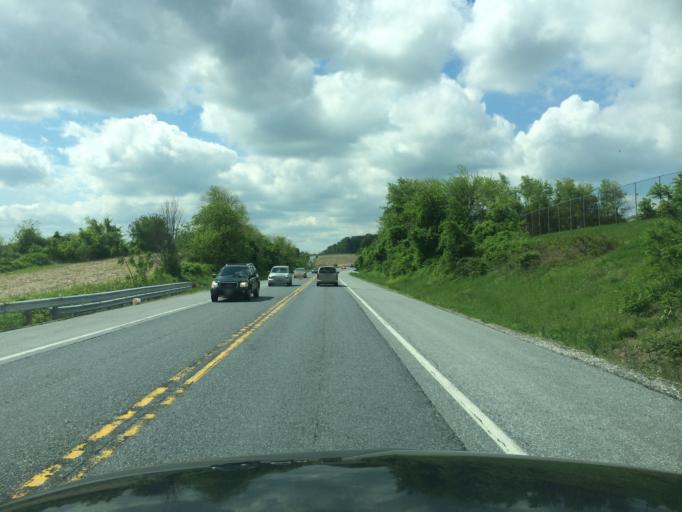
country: US
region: Maryland
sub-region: Carroll County
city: Westminster
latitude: 39.5286
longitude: -76.9884
